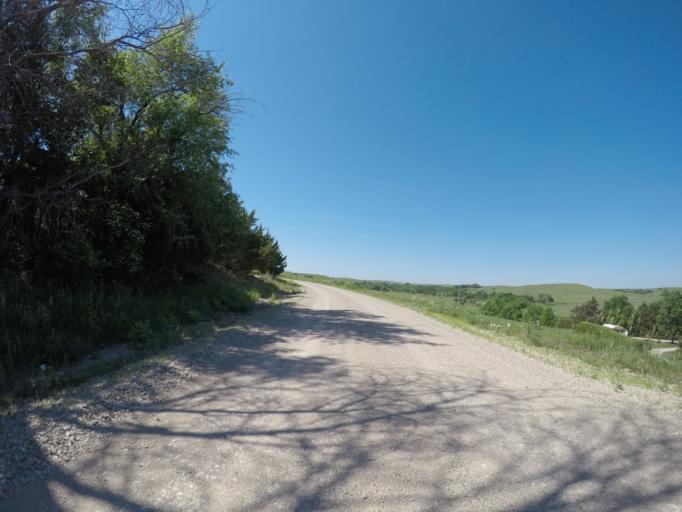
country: US
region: Kansas
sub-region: Wabaunsee County
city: Alma
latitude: 39.0170
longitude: -96.1528
